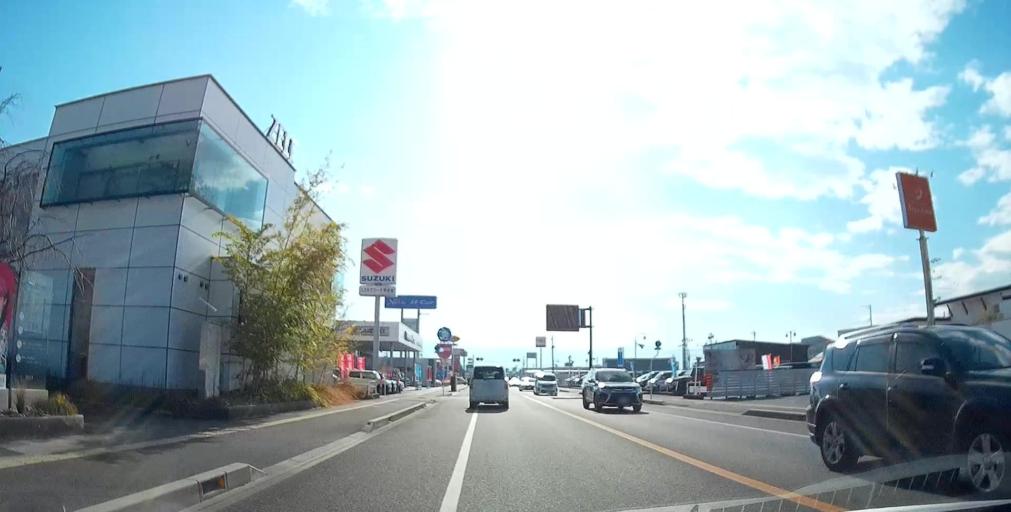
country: JP
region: Yamanashi
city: Isawa
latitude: 35.6514
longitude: 138.6134
